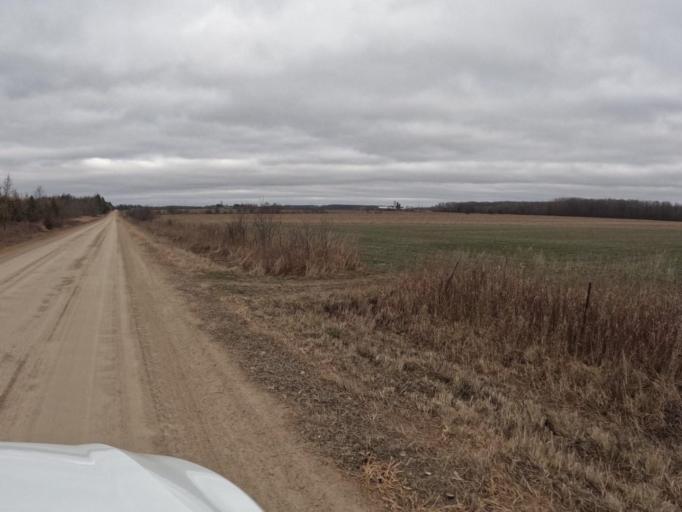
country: CA
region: Ontario
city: Shelburne
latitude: 43.9420
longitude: -80.3948
